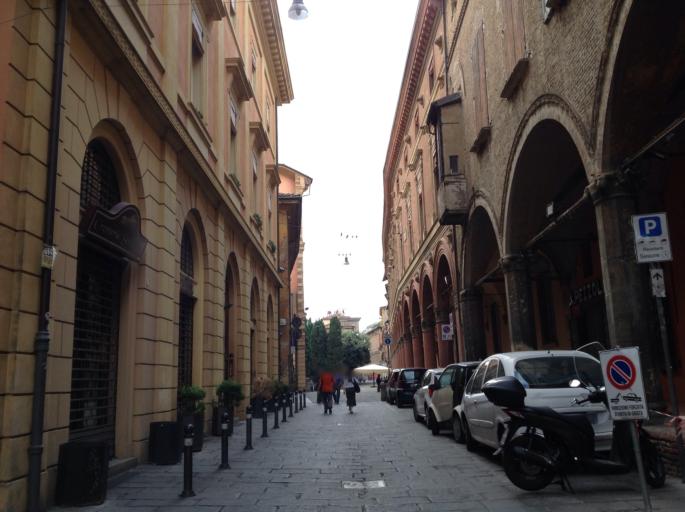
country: IT
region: Emilia-Romagna
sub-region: Provincia di Bologna
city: Bologna
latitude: 44.4931
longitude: 11.3472
